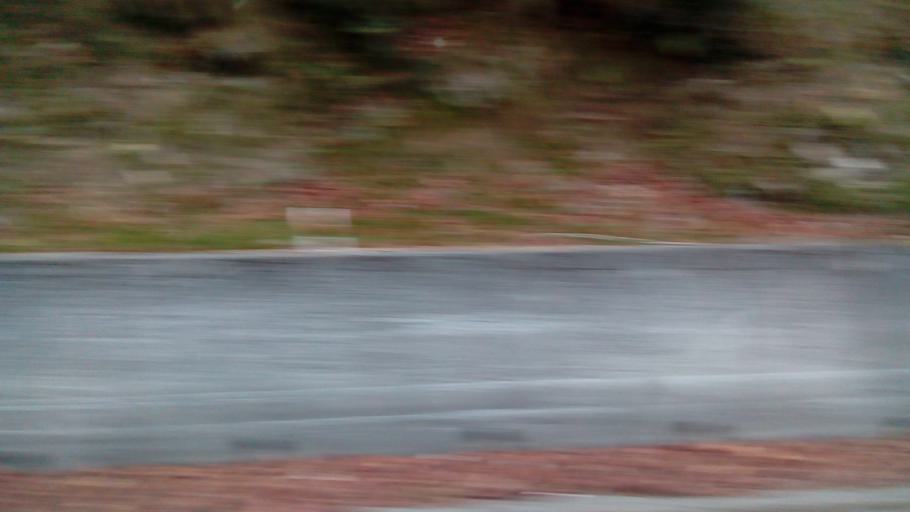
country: TW
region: Taiwan
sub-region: Hualien
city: Hualian
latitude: 24.3833
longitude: 121.3469
